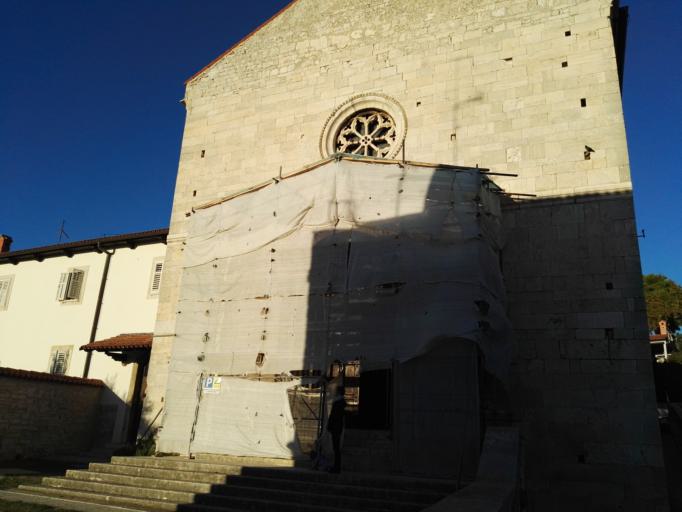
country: HR
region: Istarska
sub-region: Grad Pula
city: Pula
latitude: 44.8697
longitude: 13.8434
